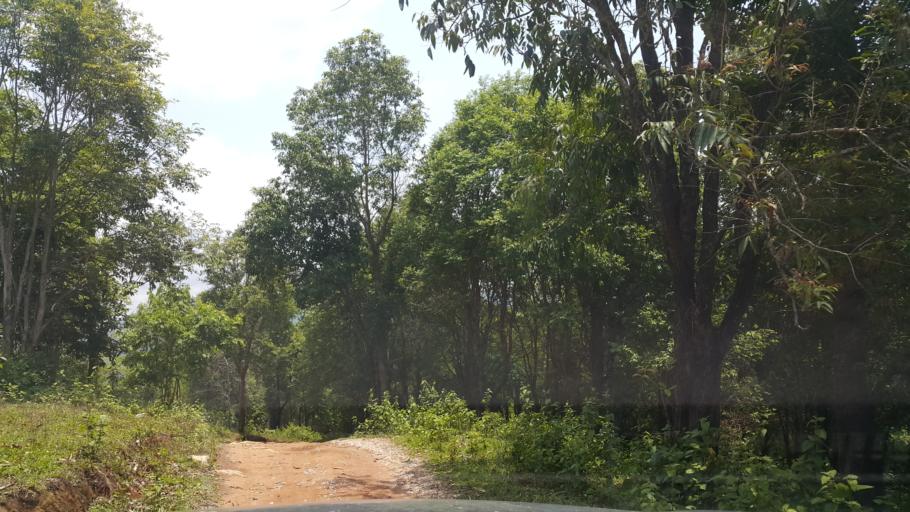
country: TH
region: Chiang Rai
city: Chiang Rai
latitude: 20.0003
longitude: 99.7006
